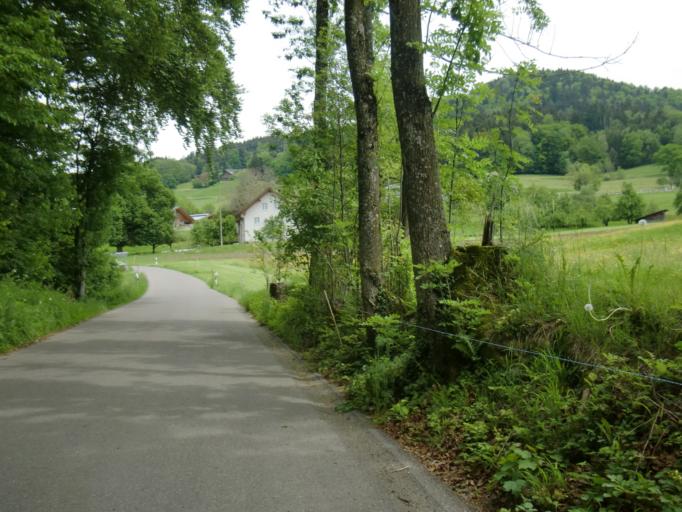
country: CH
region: Zurich
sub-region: Bezirk Hinwil
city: Hadlikon
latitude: 47.2922
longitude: 8.8653
